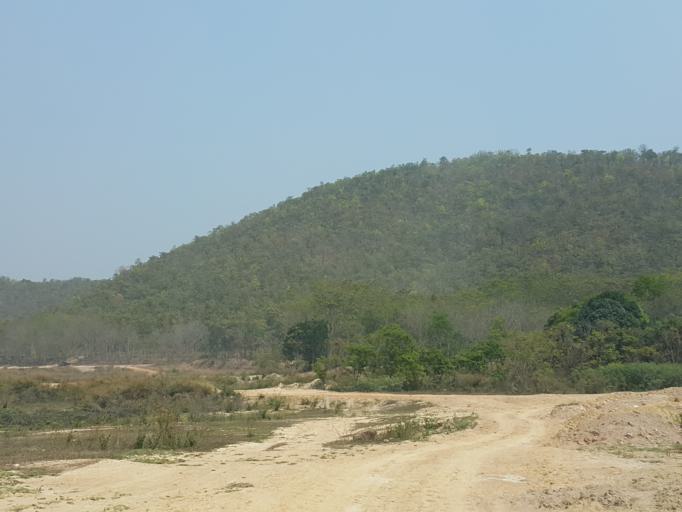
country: TH
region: Chiang Mai
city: Mae On
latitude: 18.7014
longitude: 99.2060
